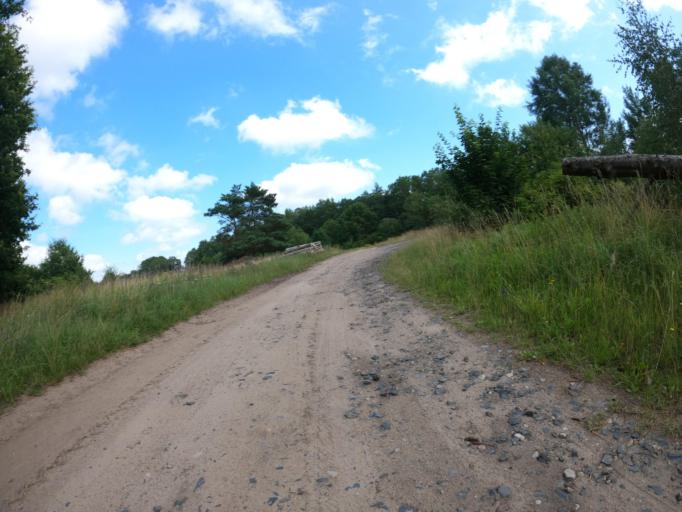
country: PL
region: West Pomeranian Voivodeship
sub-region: Powiat szczecinecki
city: Grzmiaca
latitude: 53.8212
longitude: 16.4791
